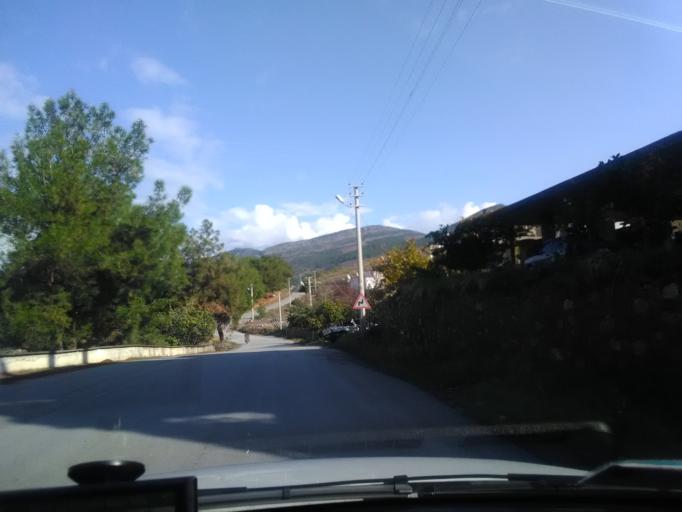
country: TR
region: Antalya
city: Gazipasa
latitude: 36.2890
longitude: 32.3249
